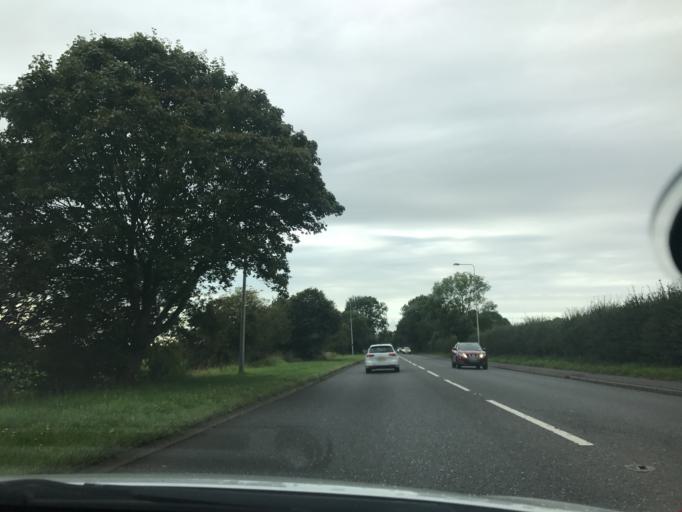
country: GB
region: England
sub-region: Cheshire West and Chester
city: Tarvin
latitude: 53.1969
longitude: -2.7864
